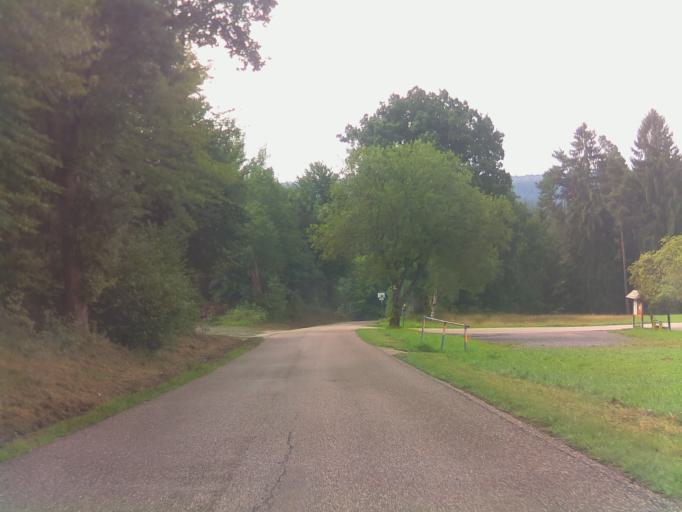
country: DE
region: Baden-Wuerttemberg
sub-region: Karlsruhe Region
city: Dobel
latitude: 48.7930
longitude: 8.5042
